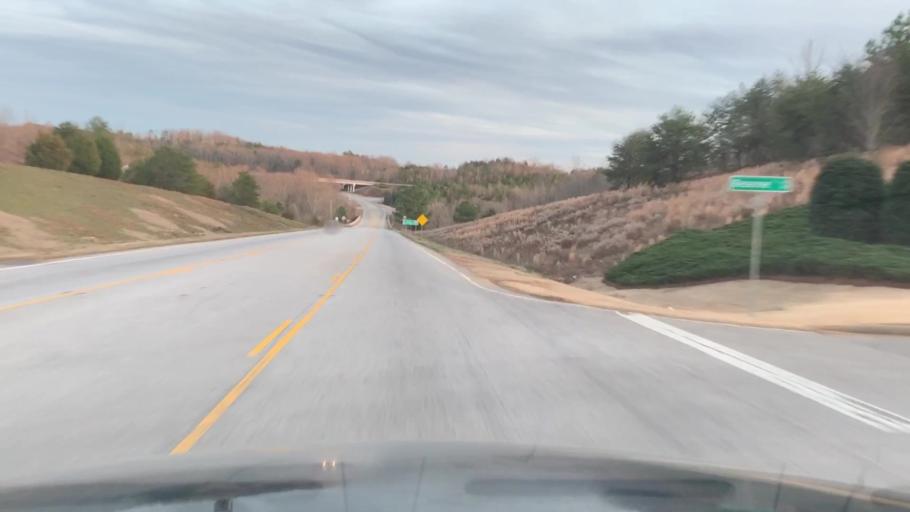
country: US
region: South Carolina
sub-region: Greenville County
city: Golden Grove
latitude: 34.7665
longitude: -82.4573
